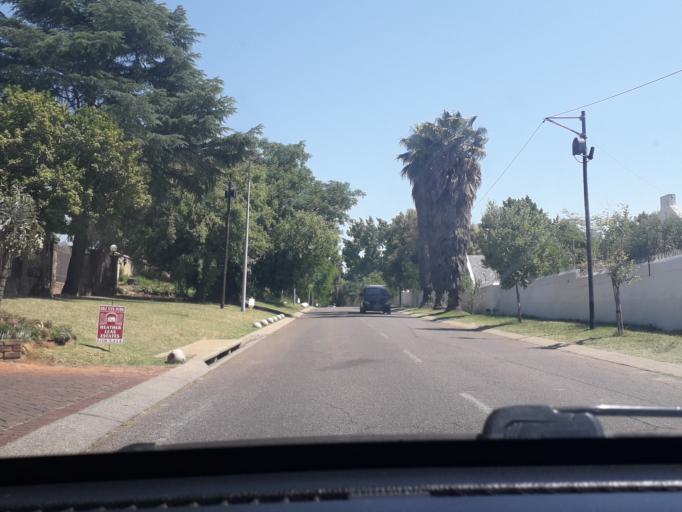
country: ZA
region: Gauteng
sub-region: City of Johannesburg Metropolitan Municipality
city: Modderfontein
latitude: -26.0947
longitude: 28.0718
